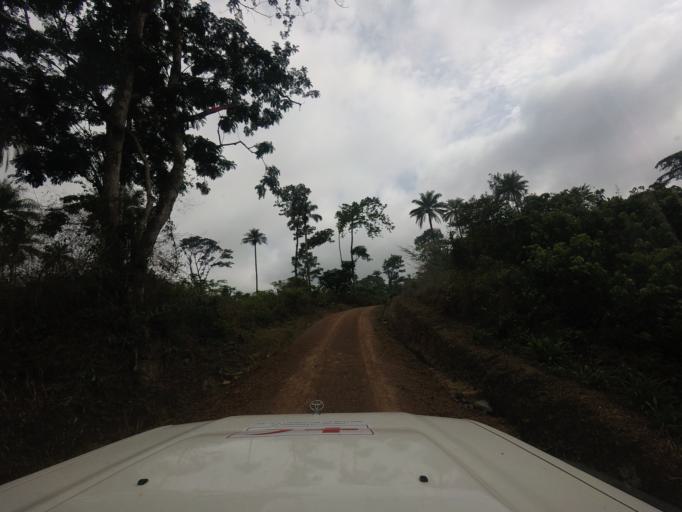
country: LR
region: Lofa
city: Voinjama
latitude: 8.4572
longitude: -9.7943
